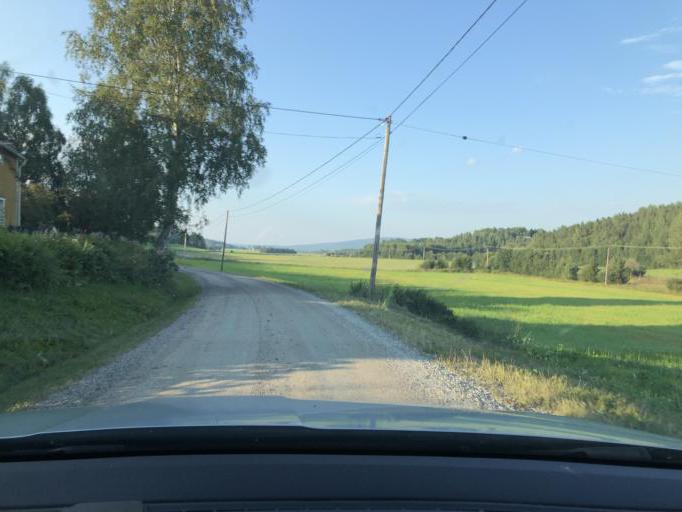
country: SE
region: Vaesternorrland
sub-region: Kramfors Kommun
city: Bollstabruk
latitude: 63.0582
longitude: 17.7328
